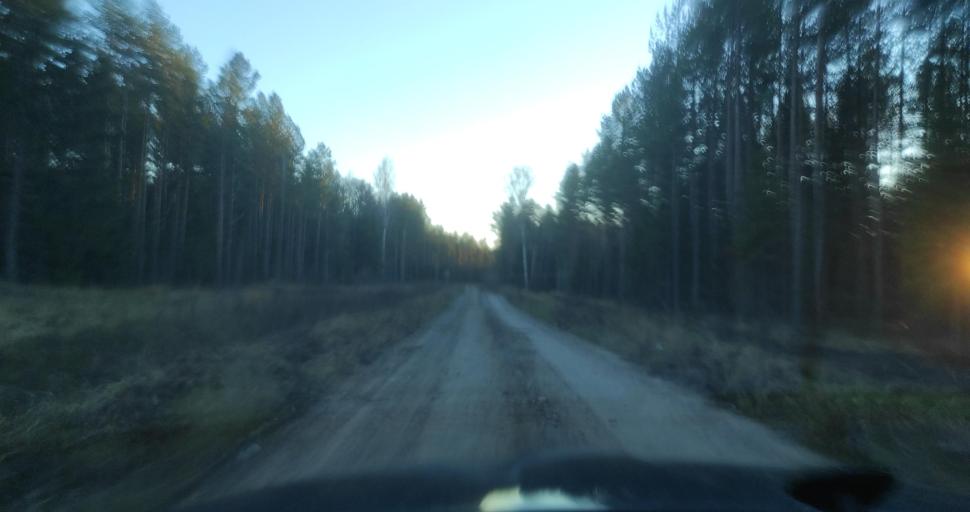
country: LV
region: Dundaga
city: Dundaga
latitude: 57.3756
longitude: 22.0792
